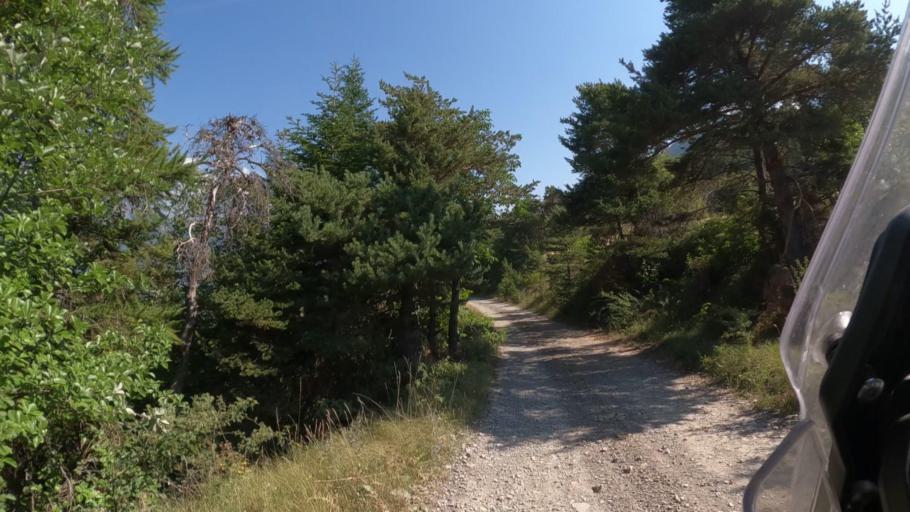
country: FR
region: Provence-Alpes-Cote d'Azur
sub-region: Departement des Hautes-Alpes
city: Embrun
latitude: 44.5883
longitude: 6.5497
